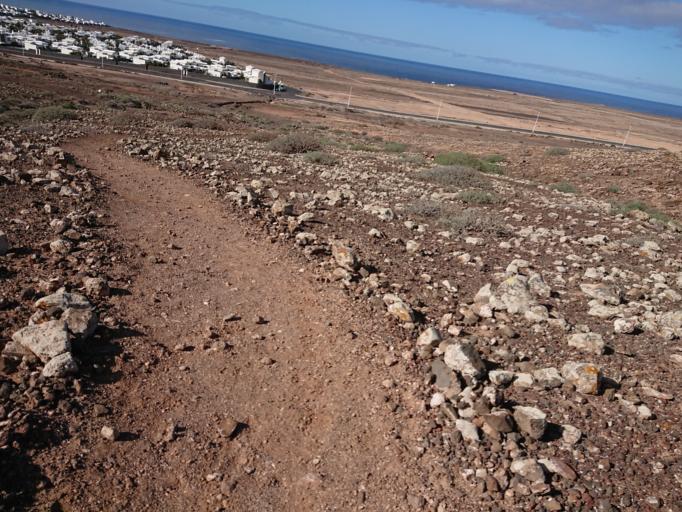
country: ES
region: Canary Islands
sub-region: Provincia de Las Palmas
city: Playa Blanca
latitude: 28.8723
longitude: -13.8610
